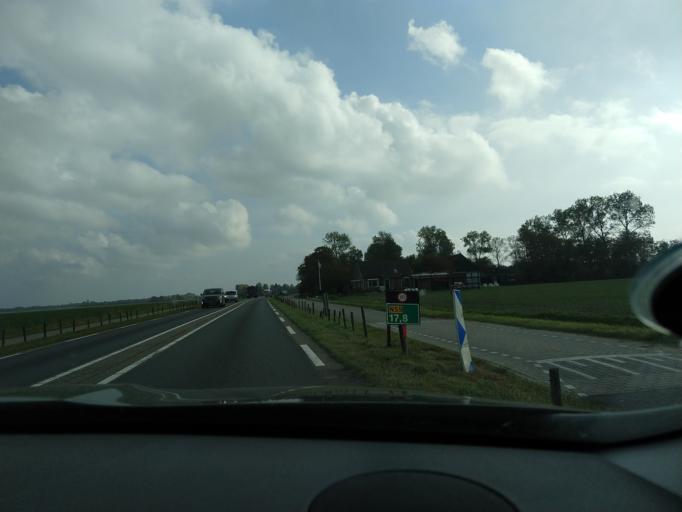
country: NL
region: Zeeland
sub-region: Schouwen-Duiveland
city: Bruinisse
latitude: 51.6492
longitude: 3.9595
